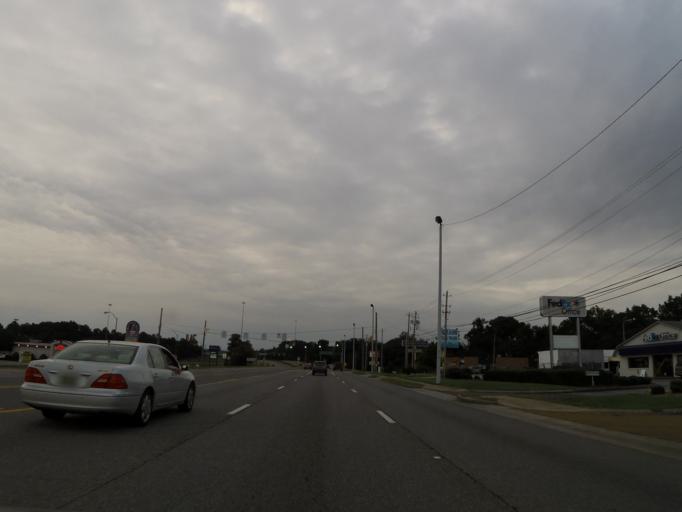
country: US
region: Alabama
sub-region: Madison County
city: Redstone Arsenal
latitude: 34.7361
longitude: -86.6493
